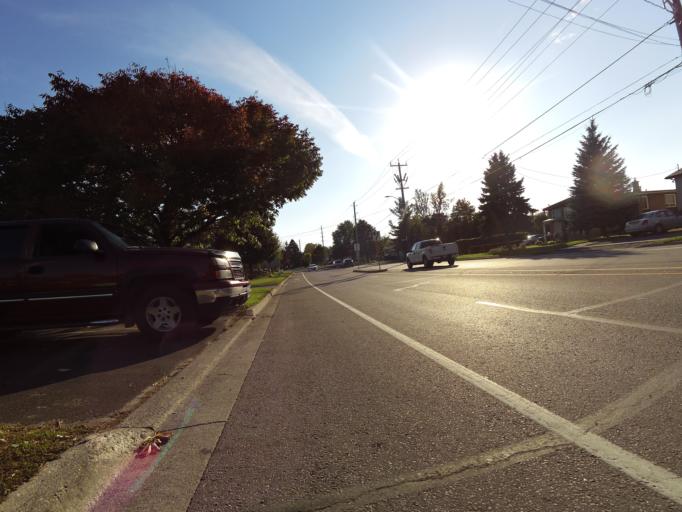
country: CA
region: Ontario
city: Kingston
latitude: 44.2716
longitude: -76.4785
